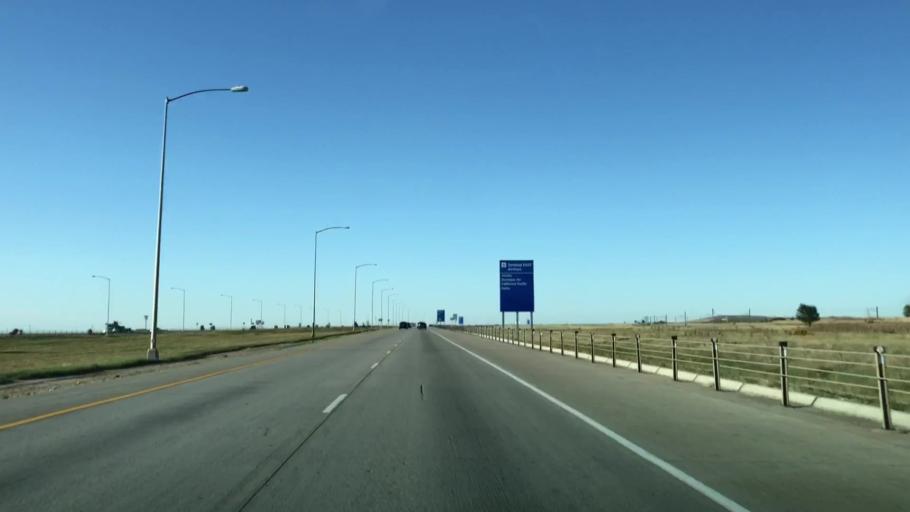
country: US
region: Colorado
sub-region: Adams County
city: Aurora
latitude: 39.8140
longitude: -104.7862
